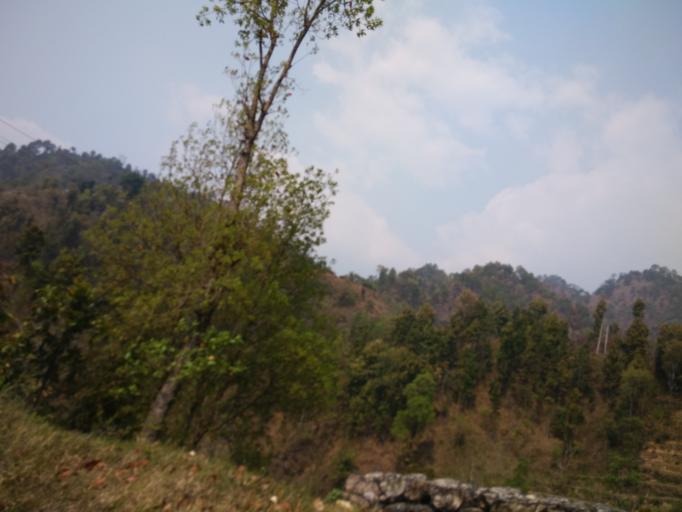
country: NP
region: Central Region
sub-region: Narayani Zone
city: Hitura
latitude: 27.5263
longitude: 85.0452
